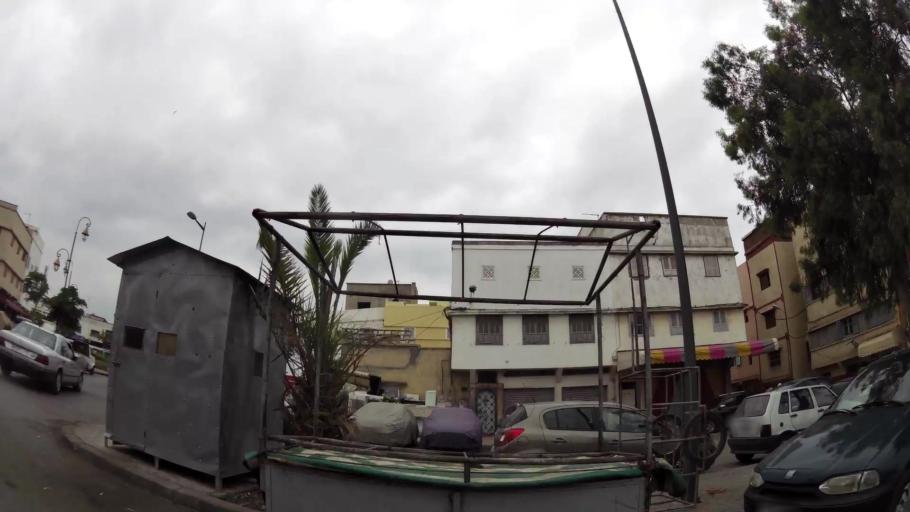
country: MA
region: Rabat-Sale-Zemmour-Zaer
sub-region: Rabat
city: Rabat
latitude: 33.9920
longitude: -6.8686
